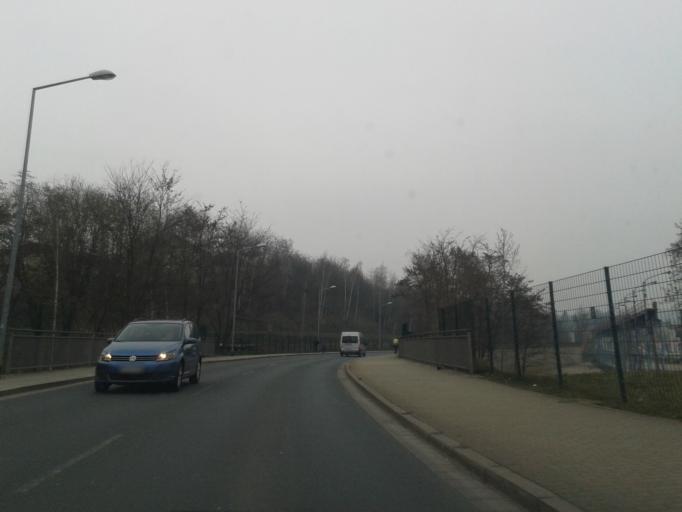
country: DE
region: Saxony
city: Freital
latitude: 51.0016
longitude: 13.6465
